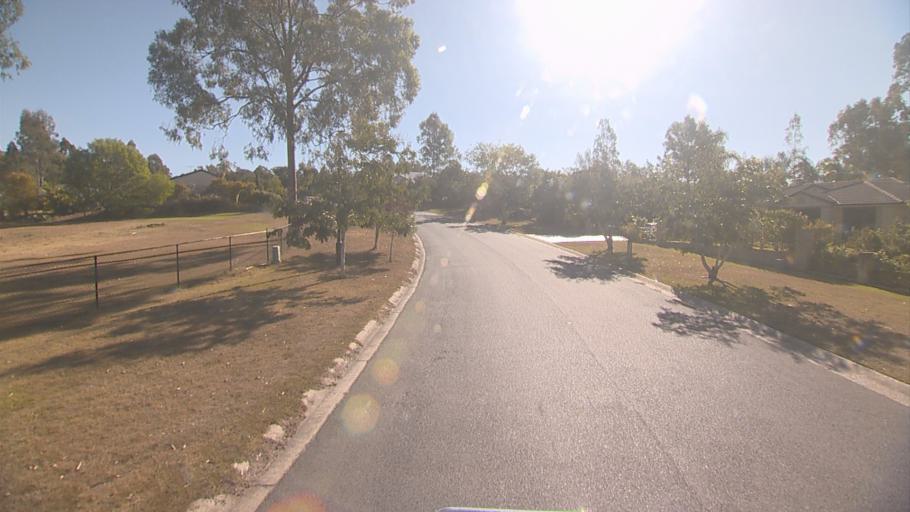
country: AU
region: Queensland
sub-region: Logan
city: Cedar Vale
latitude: -27.8687
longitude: 153.0398
